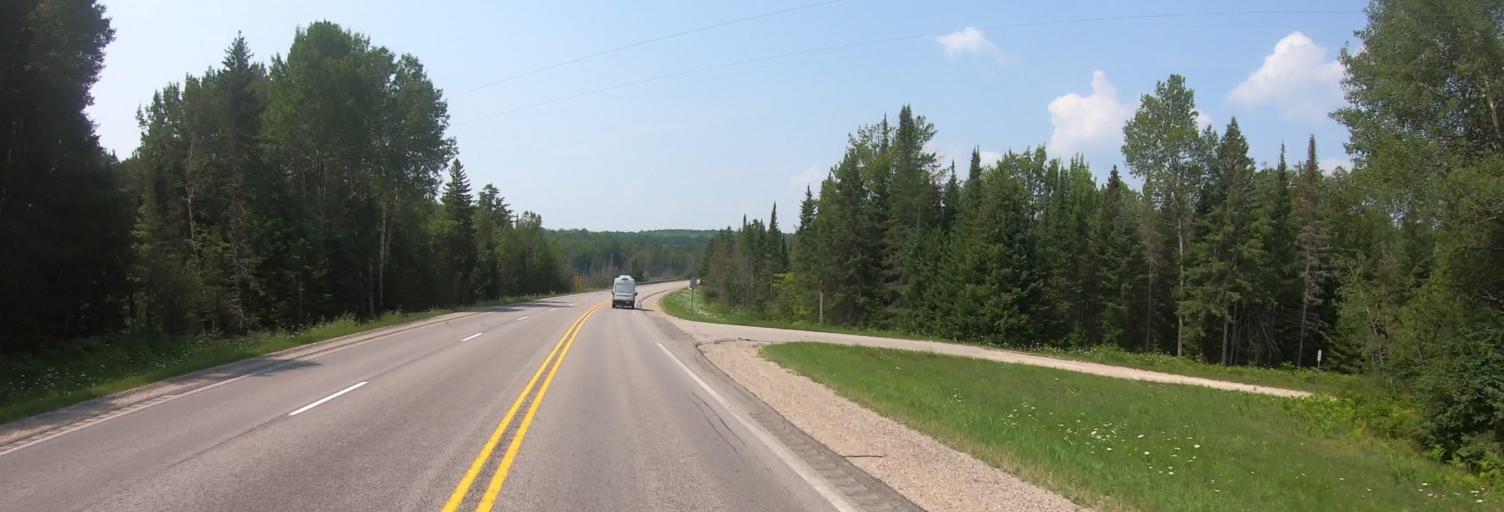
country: US
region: Michigan
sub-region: Luce County
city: Newberry
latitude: 46.3369
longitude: -85.7499
